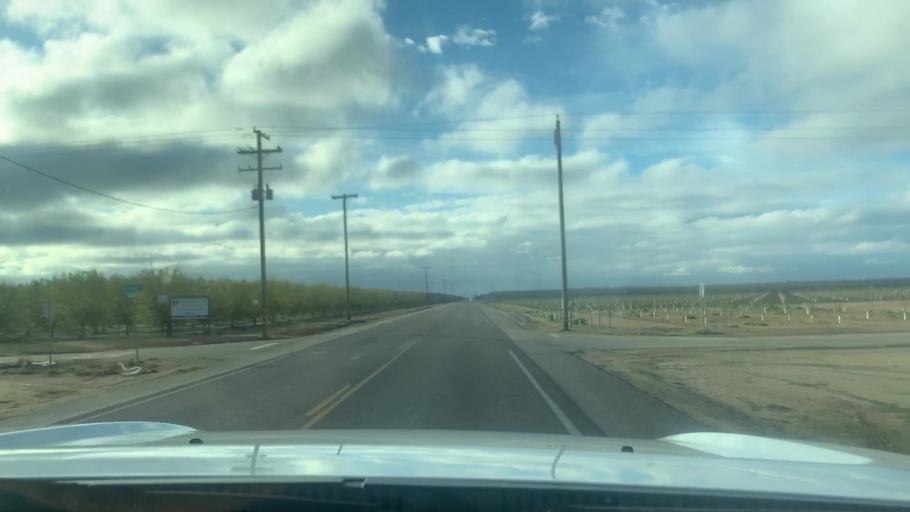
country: US
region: California
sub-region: Kern County
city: Wasco
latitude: 35.5002
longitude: -119.3855
